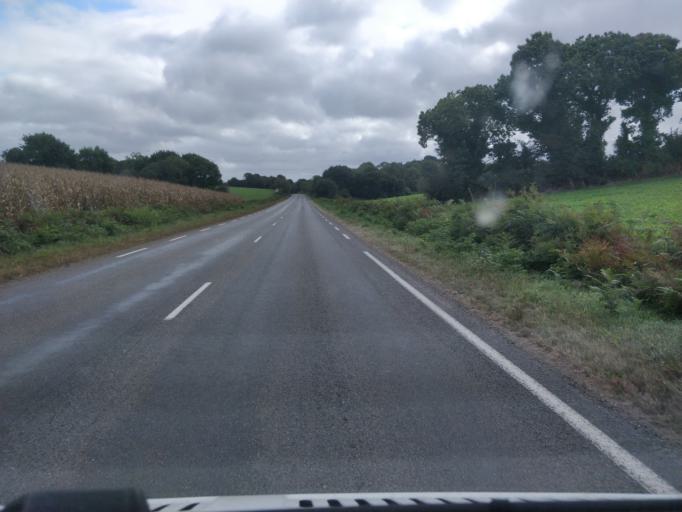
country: FR
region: Brittany
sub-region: Departement du Finistere
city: Ploneis
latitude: 47.9932
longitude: -4.2289
